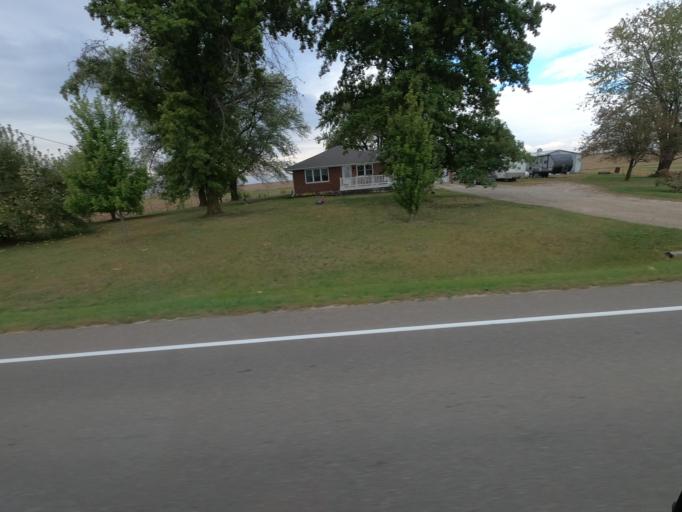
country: US
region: Iowa
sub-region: Henry County
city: Mount Pleasant
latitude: 40.7846
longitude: -91.6314
